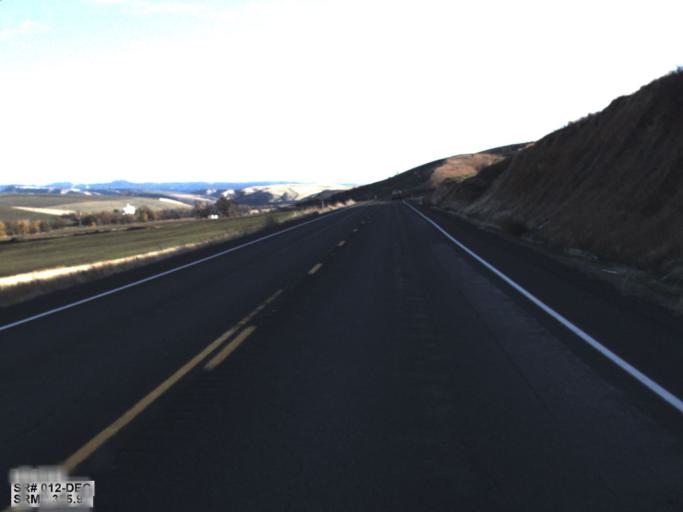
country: US
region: Washington
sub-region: Walla Walla County
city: Waitsburg
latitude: 46.2478
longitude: -118.1463
